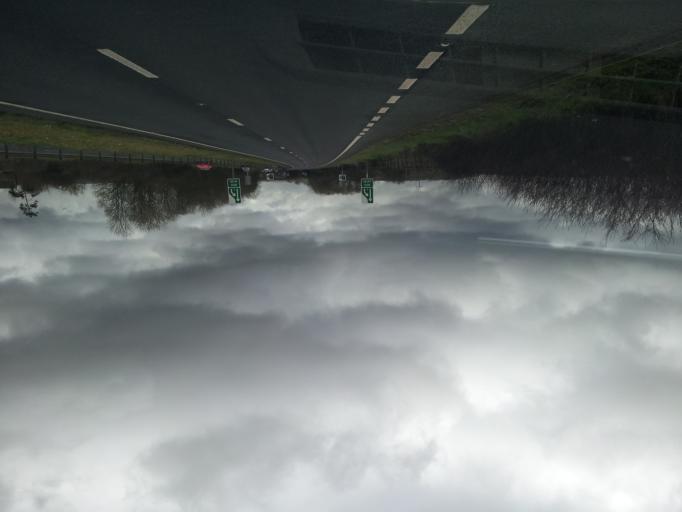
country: GB
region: England
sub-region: Somerset
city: Ilchester
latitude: 51.0244
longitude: -2.6542
